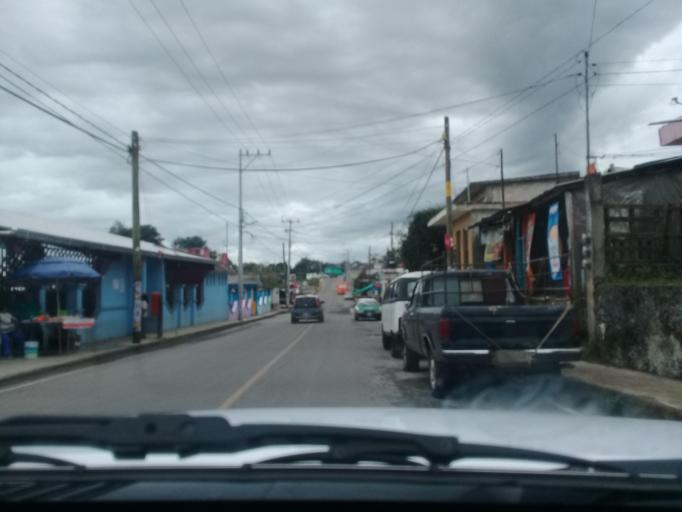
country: MX
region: Veracruz
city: Rafael Lucio
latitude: 19.5976
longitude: -96.9893
